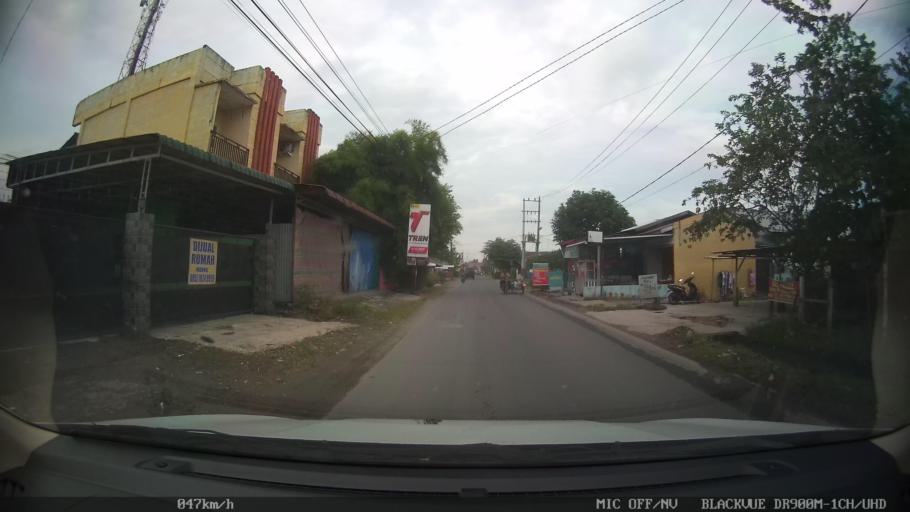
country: ID
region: North Sumatra
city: Sunggal
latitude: 3.6203
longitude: 98.6001
